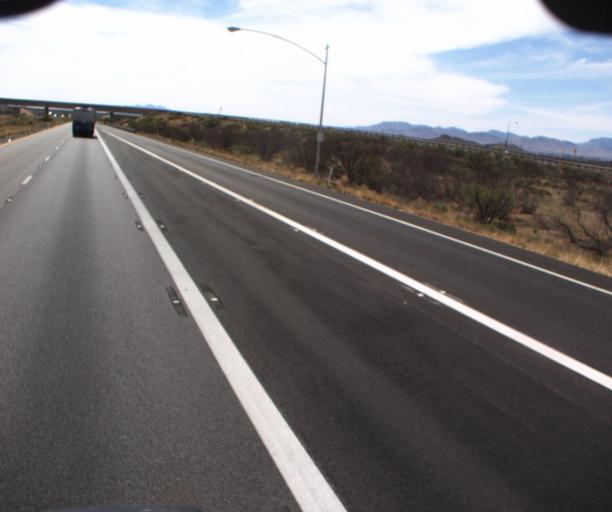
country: US
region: Arizona
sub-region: Cochise County
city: Willcox
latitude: 32.3095
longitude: -109.7947
